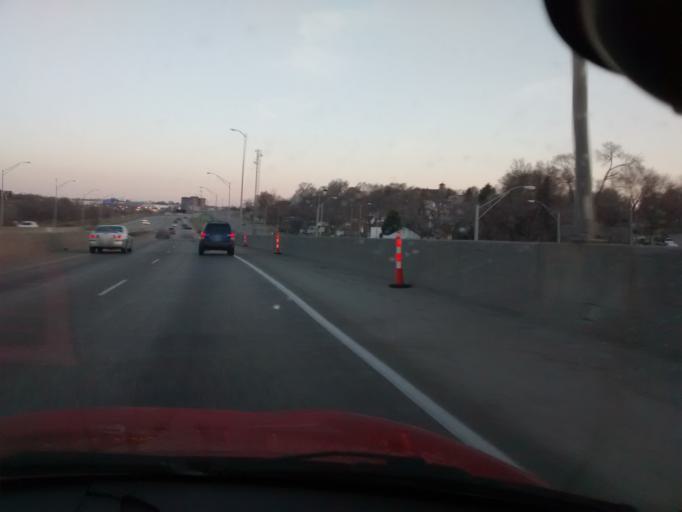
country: US
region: Nebraska
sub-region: Douglas County
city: Omaha
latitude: 41.1965
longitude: -95.9423
